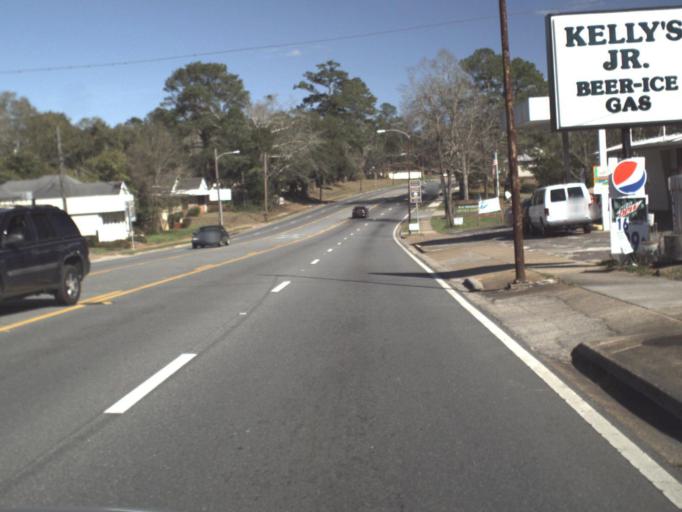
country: US
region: Florida
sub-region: Gadsden County
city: Quincy
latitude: 30.5881
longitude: -84.5731
